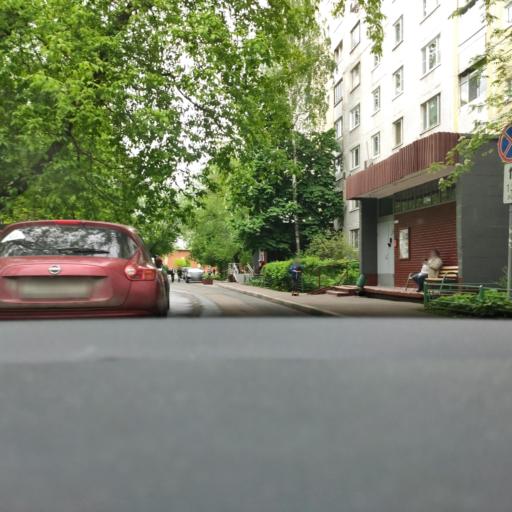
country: RU
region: Moscow
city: Bibirevo
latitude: 55.8879
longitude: 37.6175
